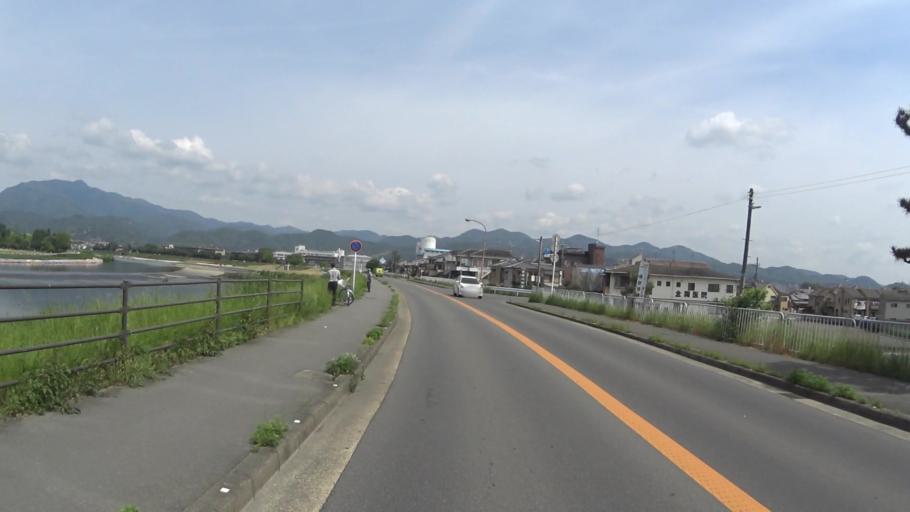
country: JP
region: Kyoto
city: Muko
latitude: 35.0060
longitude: 135.6907
